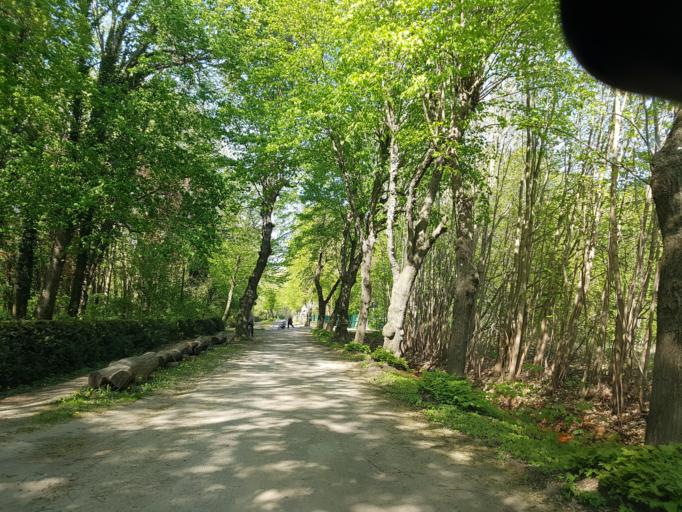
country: DE
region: Brandenburg
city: Finsterwalde
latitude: 51.6283
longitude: 13.6945
